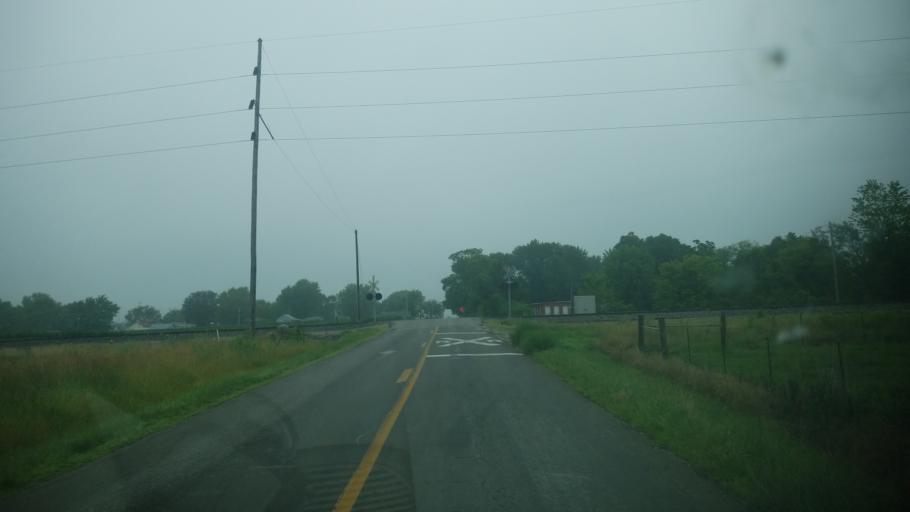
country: US
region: Missouri
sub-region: Audrain County
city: Vandalia
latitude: 39.3423
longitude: -91.3449
